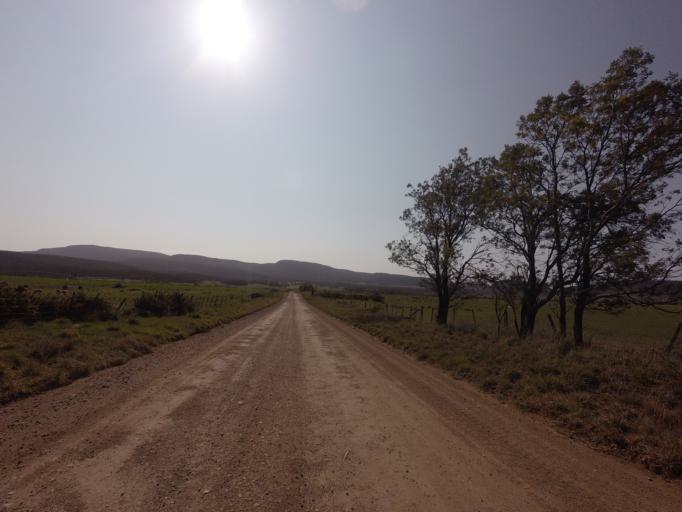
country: AU
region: Tasmania
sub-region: Break O'Day
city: St Helens
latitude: -41.8234
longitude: 147.9348
